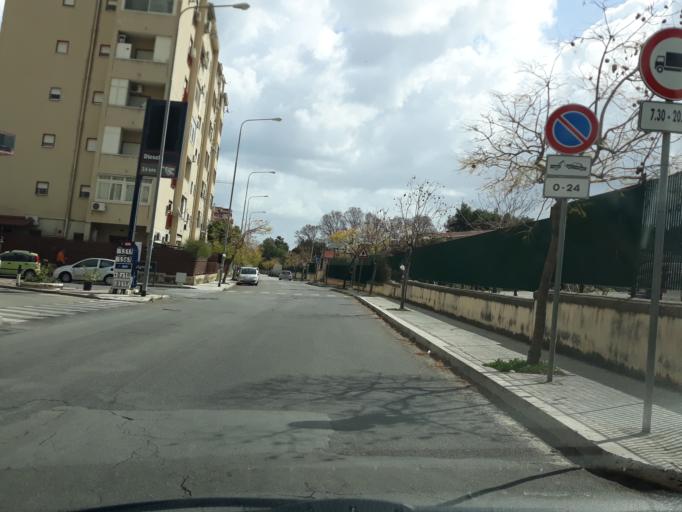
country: IT
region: Sicily
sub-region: Palermo
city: Palermo
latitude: 38.1233
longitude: 13.3208
